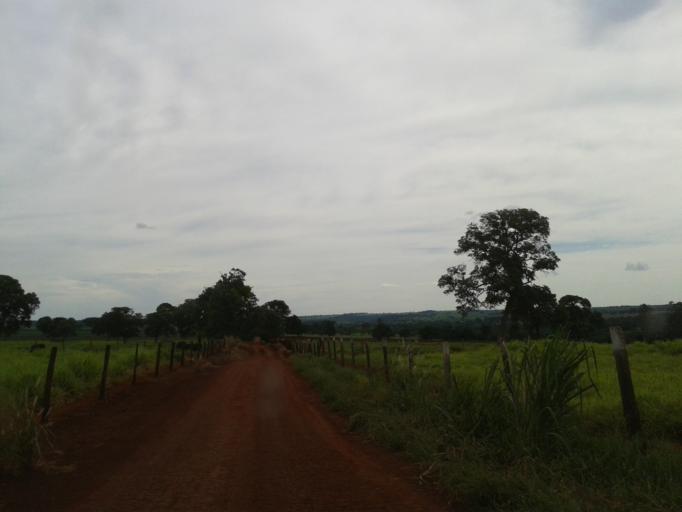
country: BR
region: Minas Gerais
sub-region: Centralina
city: Centralina
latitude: -18.6795
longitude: -49.3611
